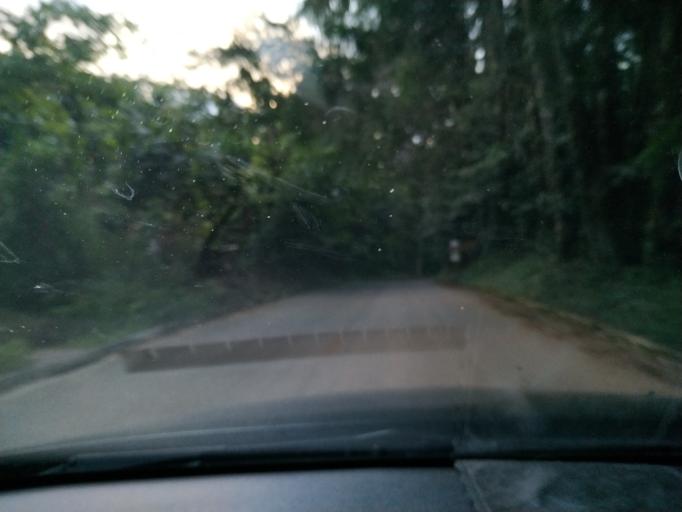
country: BR
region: Sao Paulo
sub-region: Campos Do Jordao
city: Campos do Jordao
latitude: -22.8058
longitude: -45.6353
